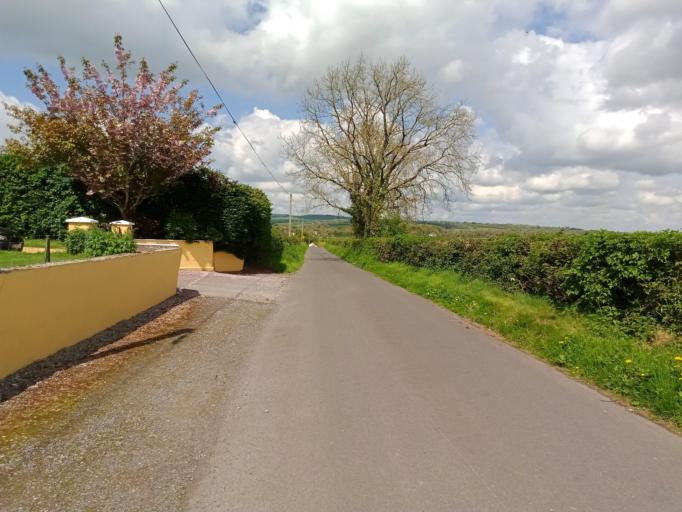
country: IE
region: Leinster
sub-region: Kilkenny
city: Ballyragget
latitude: 52.7309
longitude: -7.4180
